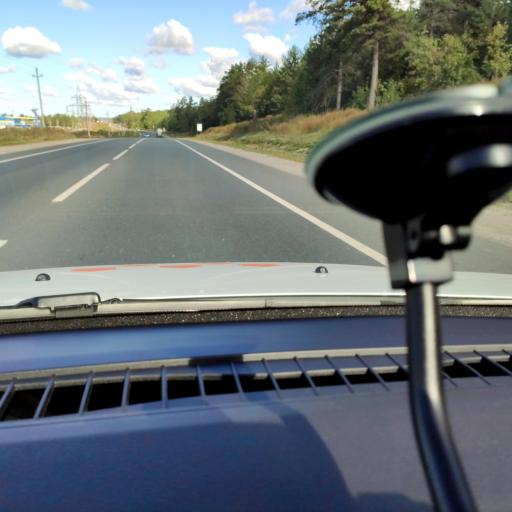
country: RU
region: Samara
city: Kurumoch
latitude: 53.4694
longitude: 50.0686
